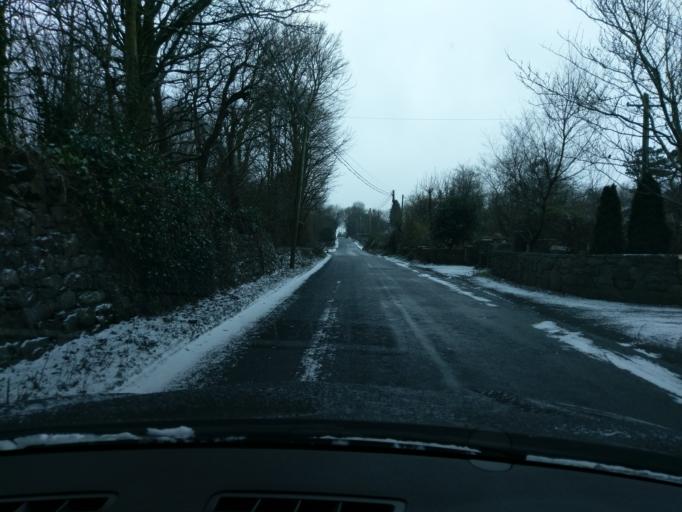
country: IE
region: Connaught
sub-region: County Galway
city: Oranmore
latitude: 53.2425
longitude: -8.8588
